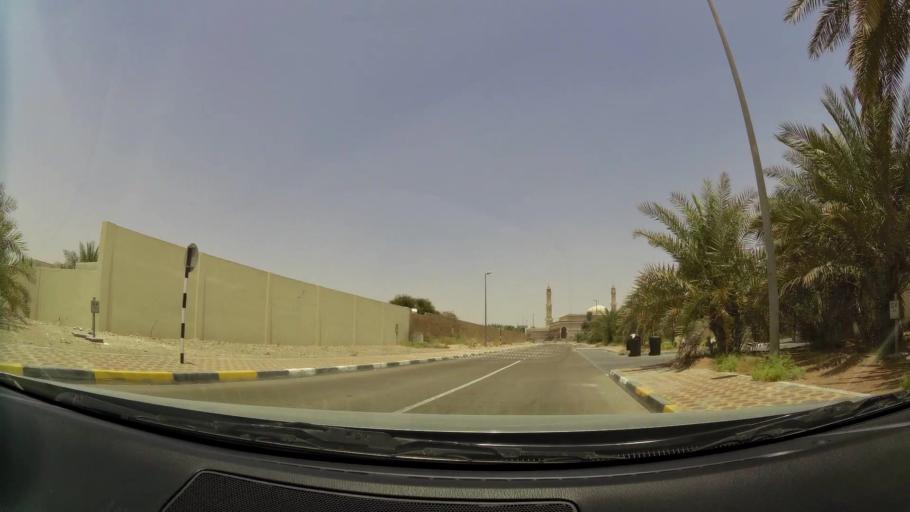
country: OM
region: Al Buraimi
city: Al Buraymi
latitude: 24.2683
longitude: 55.7067
